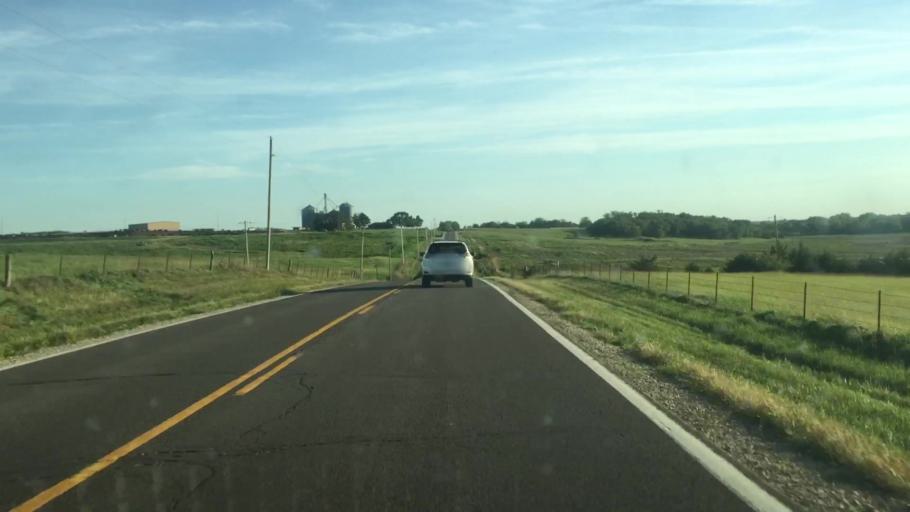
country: US
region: Kansas
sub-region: Brown County
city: Horton
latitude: 39.5813
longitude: -95.5270
